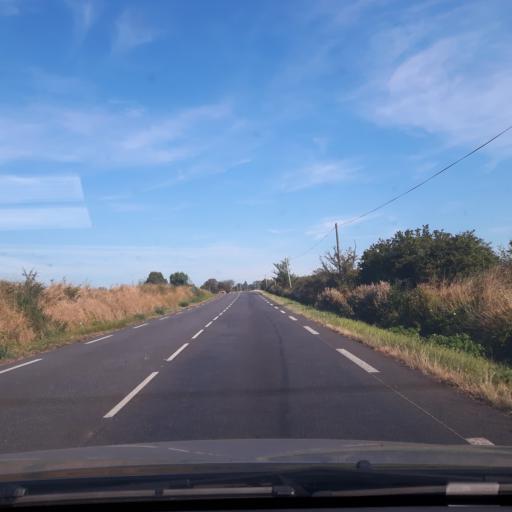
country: FR
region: Midi-Pyrenees
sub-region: Departement de la Haute-Garonne
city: Villeneuve-les-Bouloc
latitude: 43.7660
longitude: 1.4404
